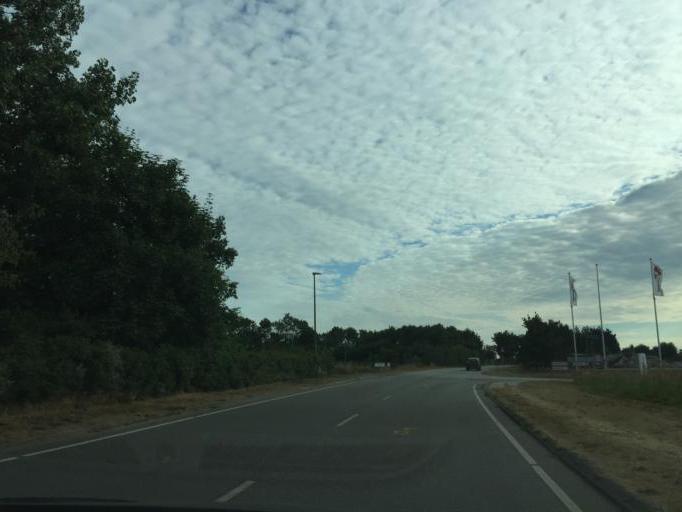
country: DK
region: South Denmark
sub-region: Assens Kommune
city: Assens
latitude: 55.2451
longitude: 9.9657
